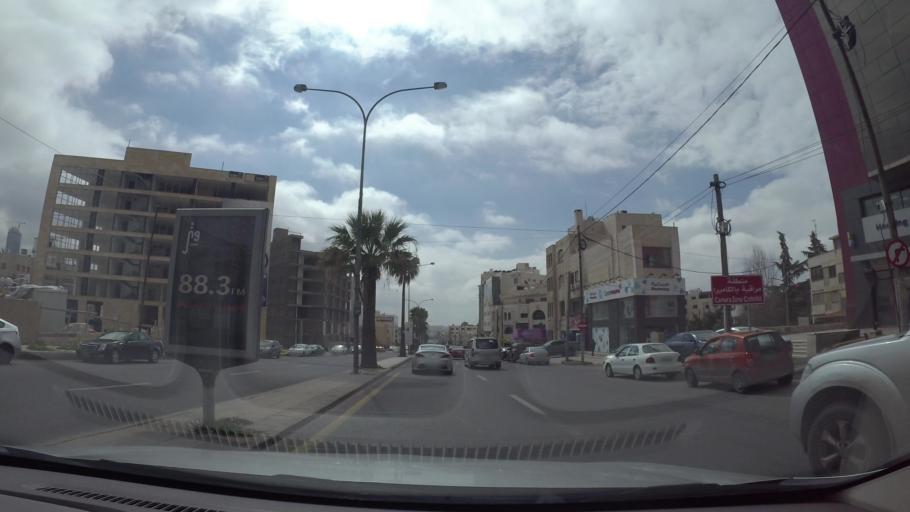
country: JO
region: Amman
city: Wadi as Sir
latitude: 31.9673
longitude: 35.8552
